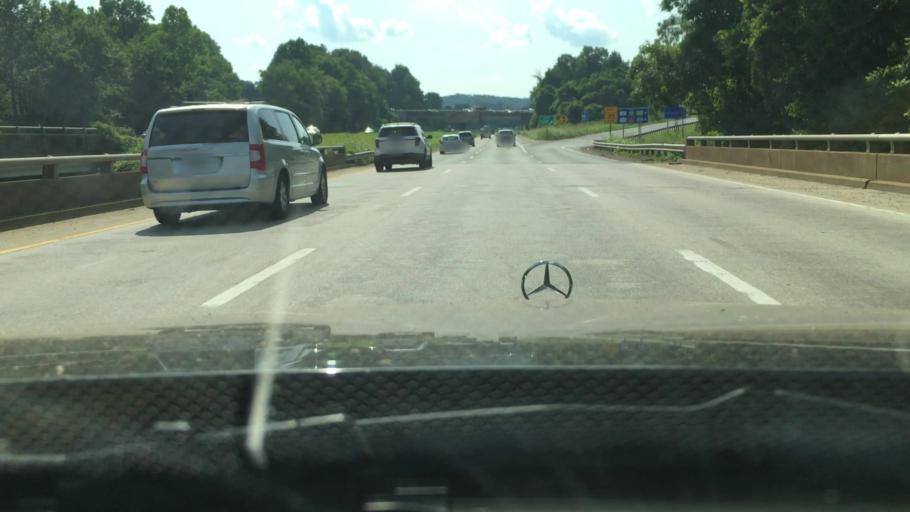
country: US
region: Virginia
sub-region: City of Charlottesville
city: Charlottesville
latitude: 38.0081
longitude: -78.5050
